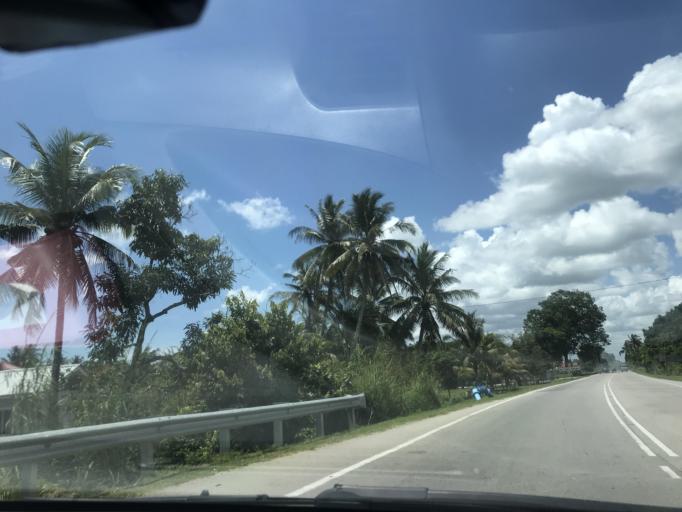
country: MY
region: Kelantan
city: Tumpat
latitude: 6.1970
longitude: 102.1341
